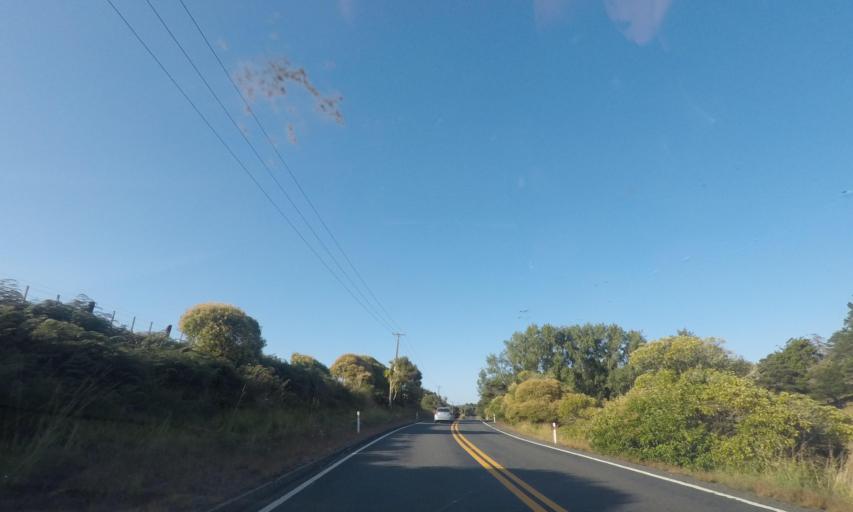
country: NZ
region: Auckland
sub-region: Auckland
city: Muriwai Beach
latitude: -36.7814
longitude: 174.4817
